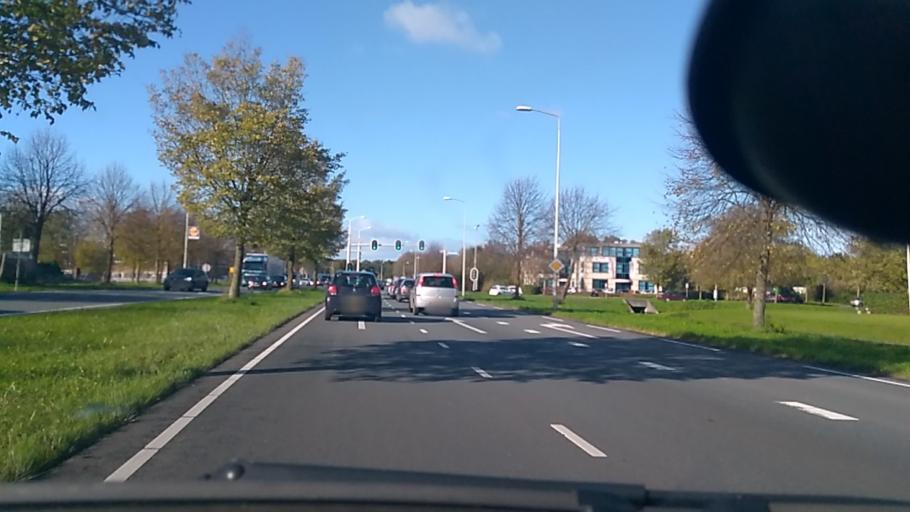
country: NL
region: North Holland
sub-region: Gemeente Hoorn
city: Hoorn
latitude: 52.6452
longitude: 5.0833
